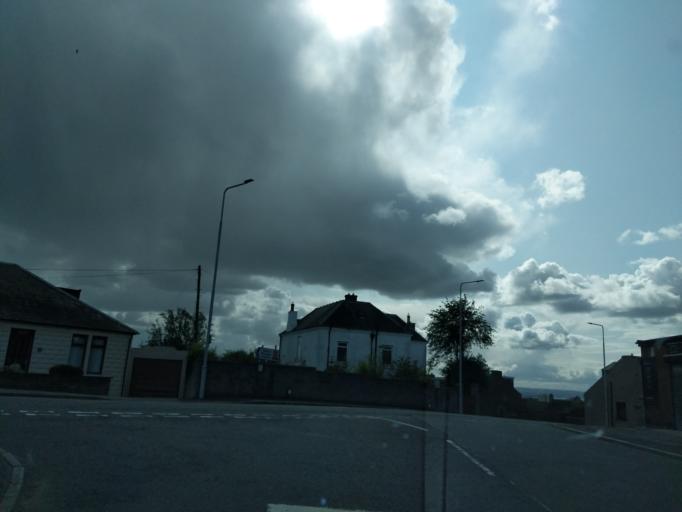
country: GB
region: Scotland
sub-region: Fife
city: Townhill
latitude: 56.0833
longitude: -3.4458
